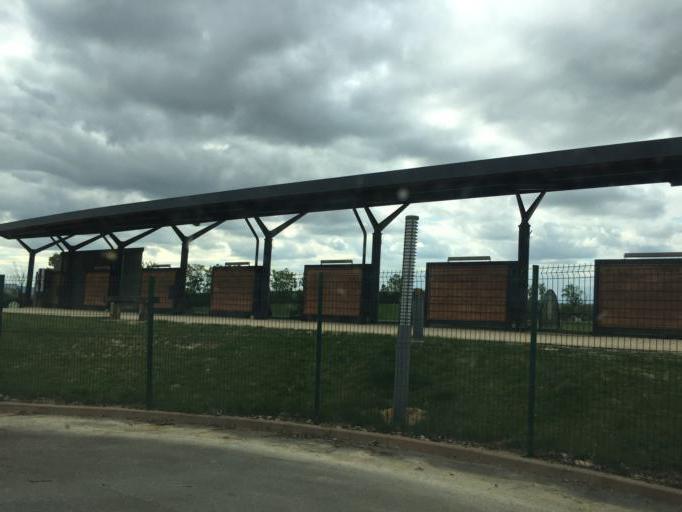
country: FR
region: Rhone-Alpes
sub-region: Departement de l'Ain
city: Tramoyes
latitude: 45.8962
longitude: 4.9661
